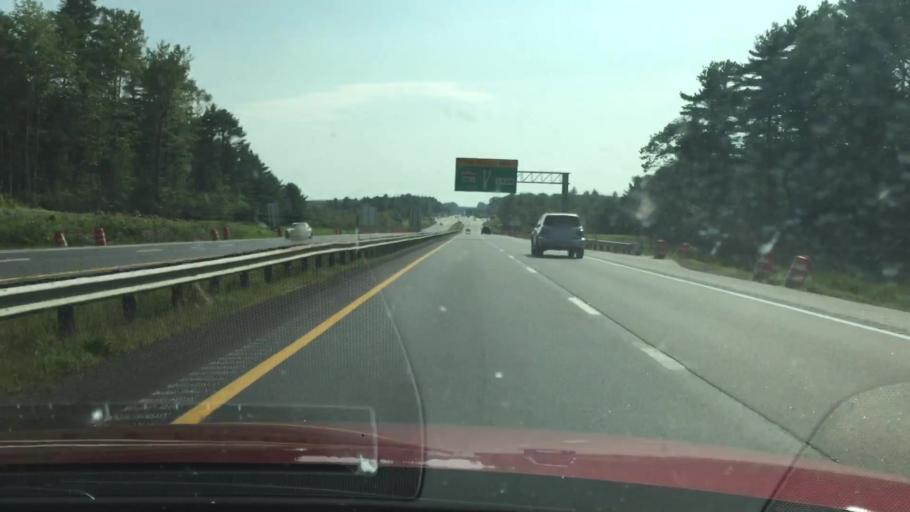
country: US
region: Maine
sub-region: Kennebec County
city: Gardiner
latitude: 44.1963
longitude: -69.8443
